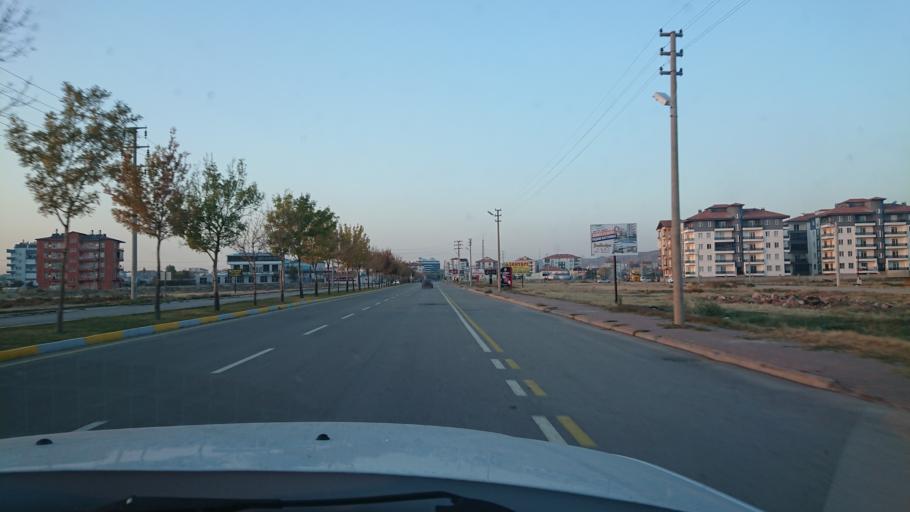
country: TR
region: Aksaray
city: Aksaray
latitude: 38.3494
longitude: 34.0438
